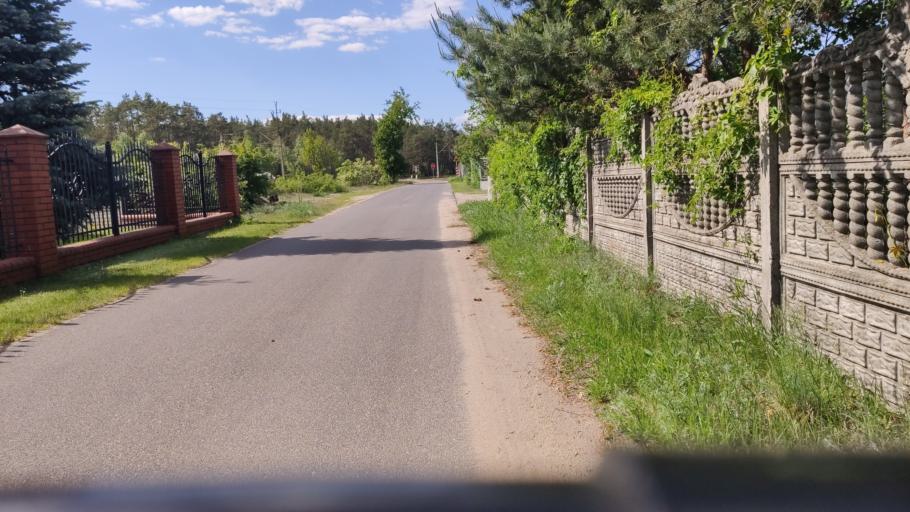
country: PL
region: Kujawsko-Pomorskie
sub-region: Wloclawek
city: Wloclawek
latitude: 52.6041
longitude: 19.0768
